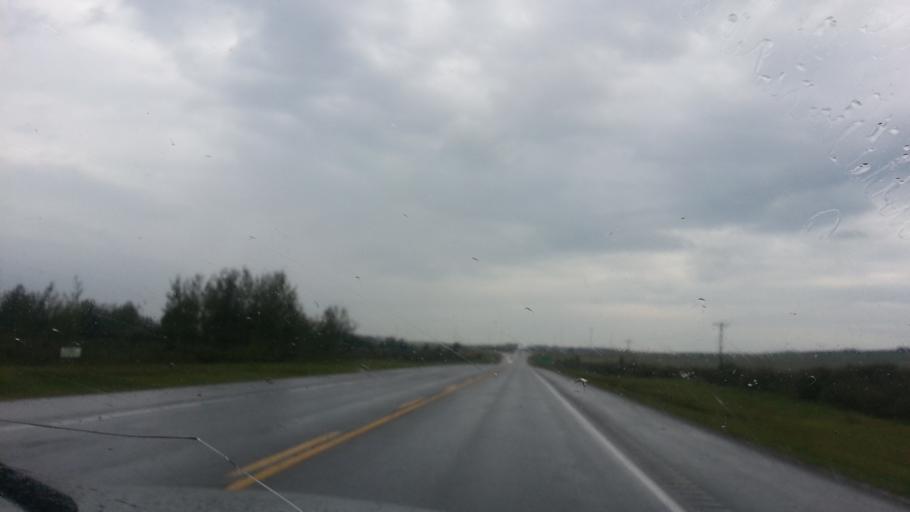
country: CA
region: Alberta
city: Cochrane
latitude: 51.0751
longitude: -114.4668
